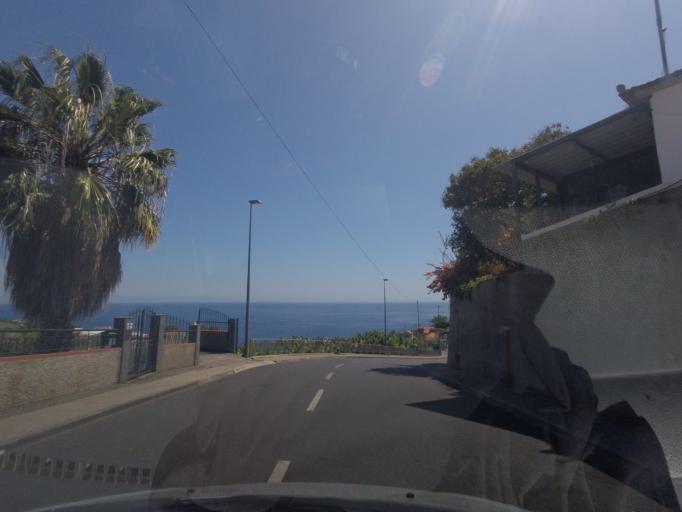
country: PT
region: Madeira
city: Camara de Lobos
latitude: 32.6477
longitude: -16.9617
